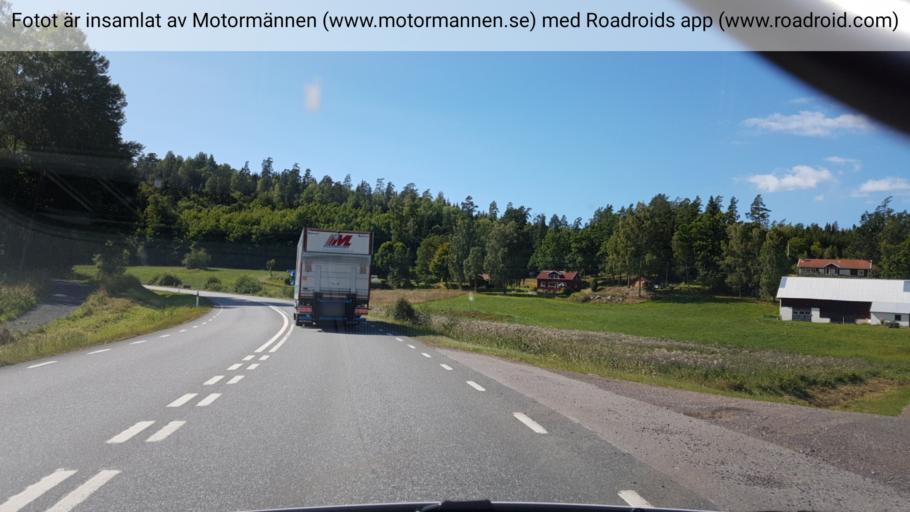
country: SE
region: Joenkoeping
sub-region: Jonkopings Kommun
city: Graenna
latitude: 58.0131
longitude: 14.5244
